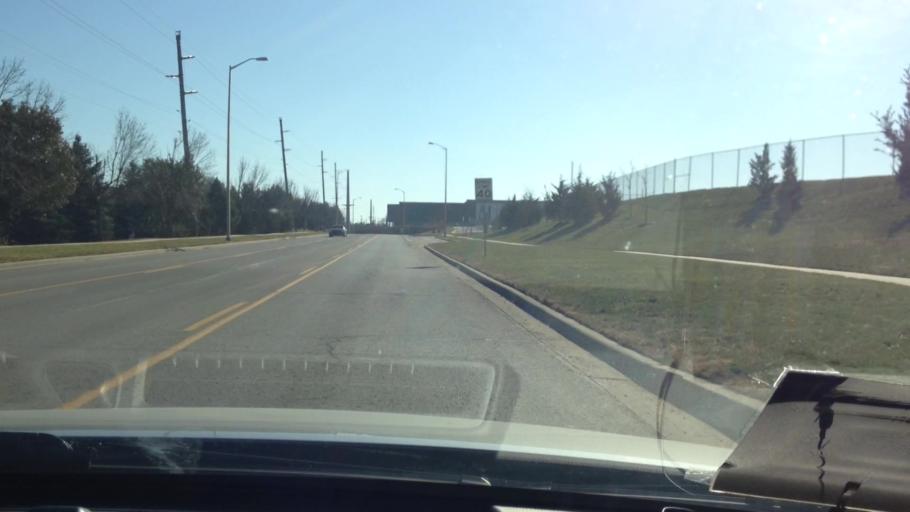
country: US
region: Kansas
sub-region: Johnson County
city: Olathe
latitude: 38.8904
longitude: -94.8531
